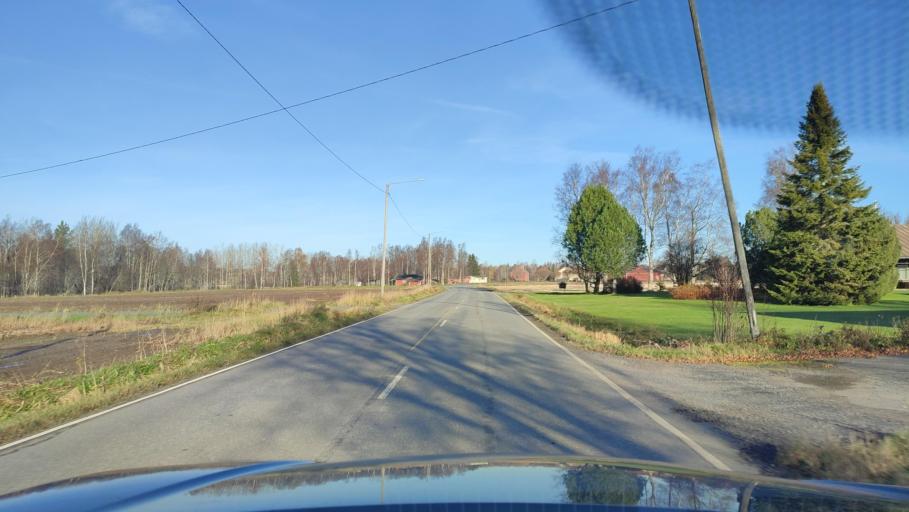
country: FI
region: Southern Ostrobothnia
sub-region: Suupohja
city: Karijoki
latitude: 62.2734
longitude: 21.7077
